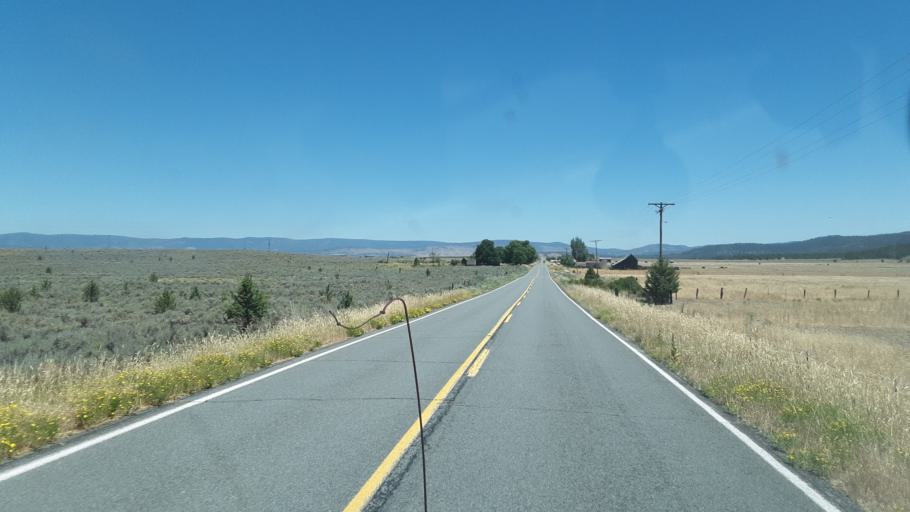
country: US
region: California
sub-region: Shasta County
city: Burney
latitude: 41.1321
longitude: -121.0876
